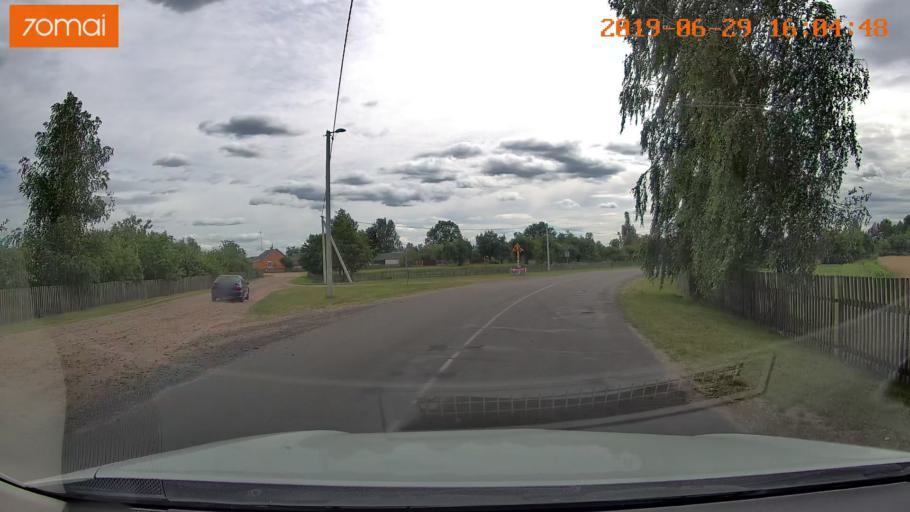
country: BY
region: Brest
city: Luninyets
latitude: 52.2197
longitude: 27.0243
